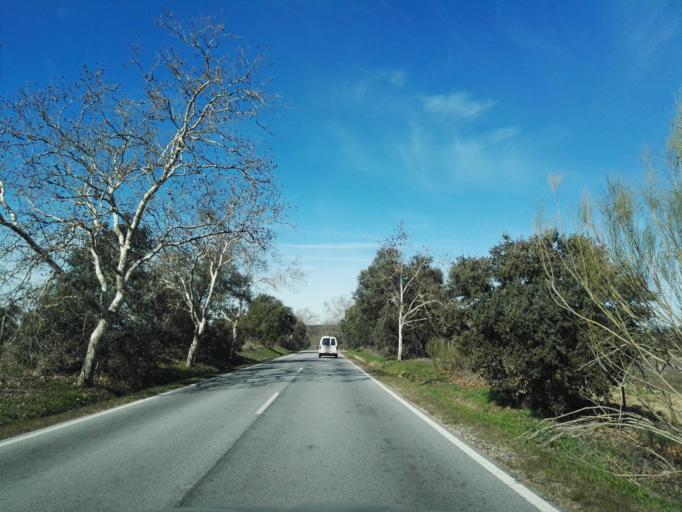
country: PT
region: Portalegre
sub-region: Arronches
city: Arronches
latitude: 39.0477
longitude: -7.2643
